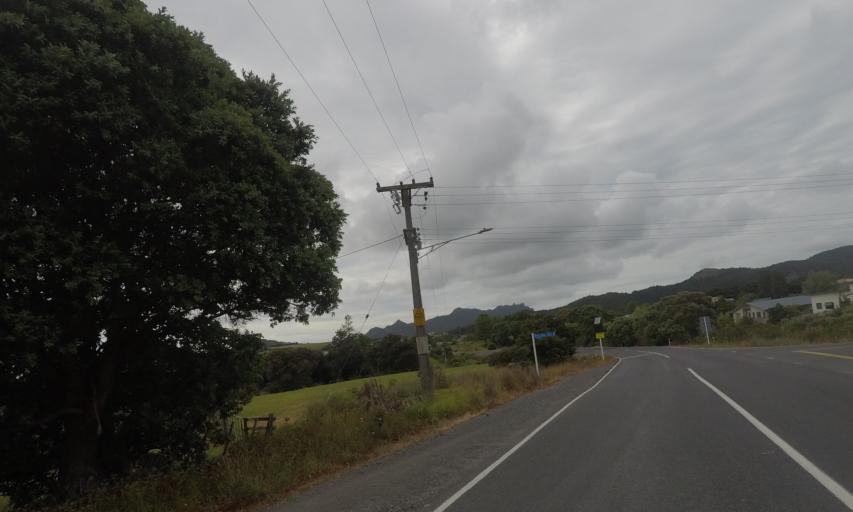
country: NZ
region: Northland
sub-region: Whangarei
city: Ruakaka
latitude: -35.7684
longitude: 174.4772
